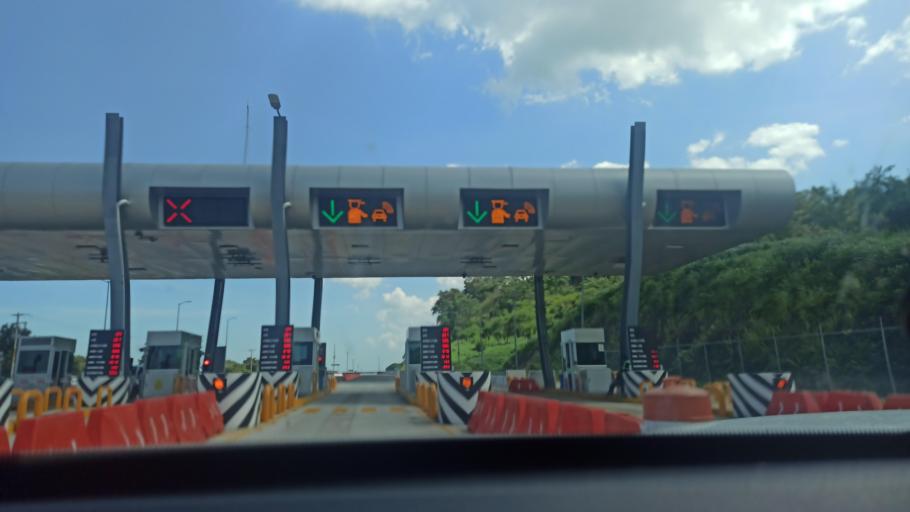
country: MX
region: Veracruz
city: Vega de Alatorre
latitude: 20.0442
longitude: -96.6846
